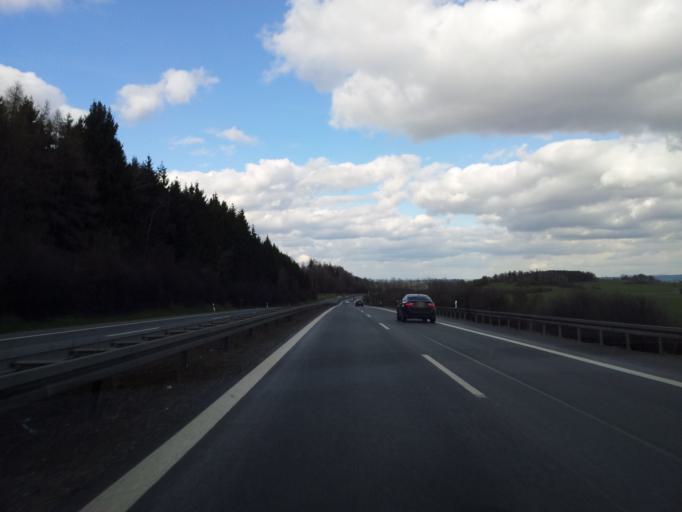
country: DE
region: Bavaria
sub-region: Upper Franconia
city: Trogen
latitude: 50.3995
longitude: 12.0132
